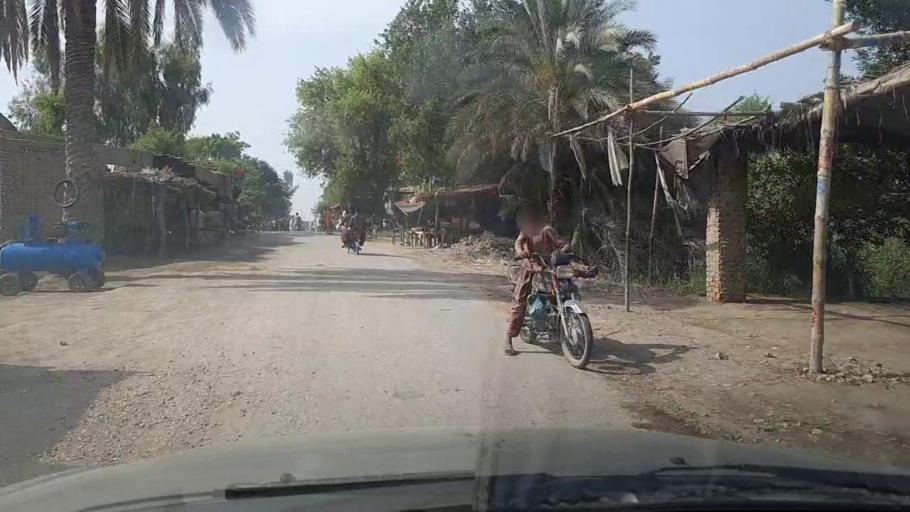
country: PK
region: Sindh
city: Gambat
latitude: 27.4517
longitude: 68.4861
